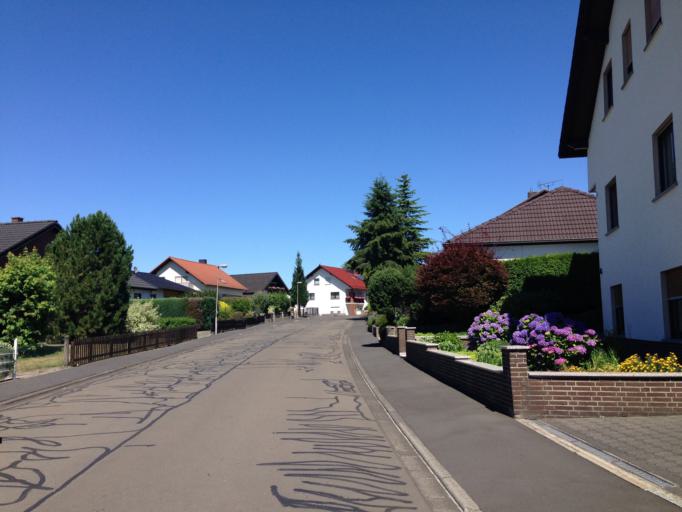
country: DE
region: Hesse
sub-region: Regierungsbezirk Giessen
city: Reiskirchen
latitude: 50.5951
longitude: 8.8277
